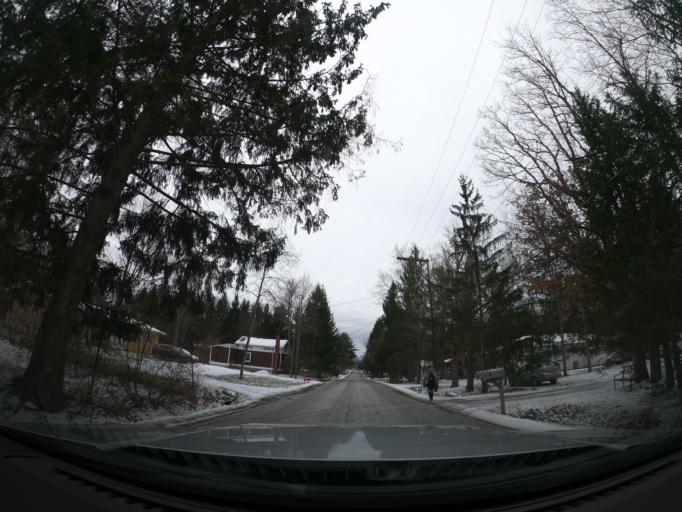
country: US
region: New York
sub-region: Tompkins County
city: Northeast Ithaca
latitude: 42.4719
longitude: -76.4503
